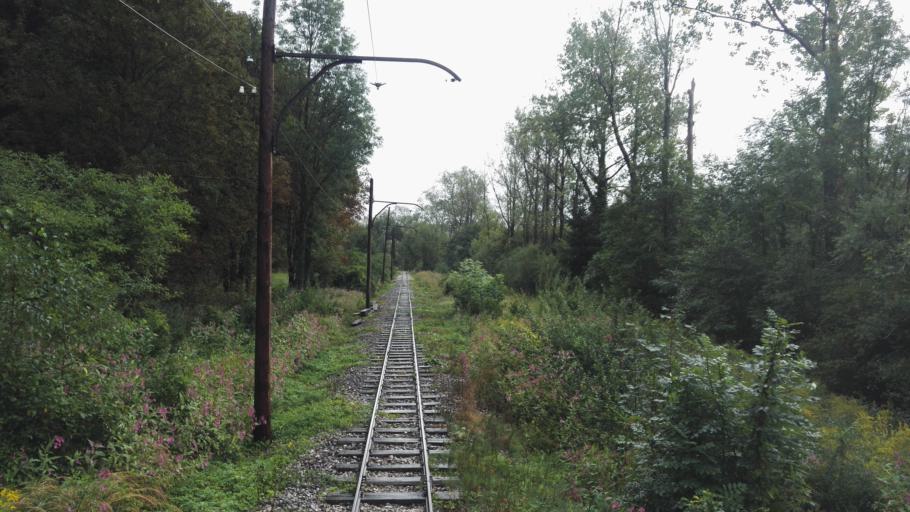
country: AT
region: Lower Austria
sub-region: Politischer Bezirk Neunkirchen
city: Reichenau an der Rax
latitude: 47.7042
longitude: 15.8257
